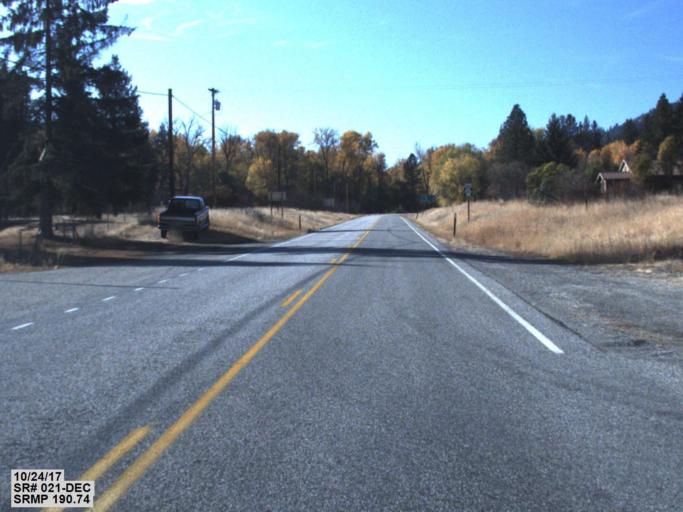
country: CA
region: British Columbia
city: Grand Forks
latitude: 48.9919
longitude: -118.5084
